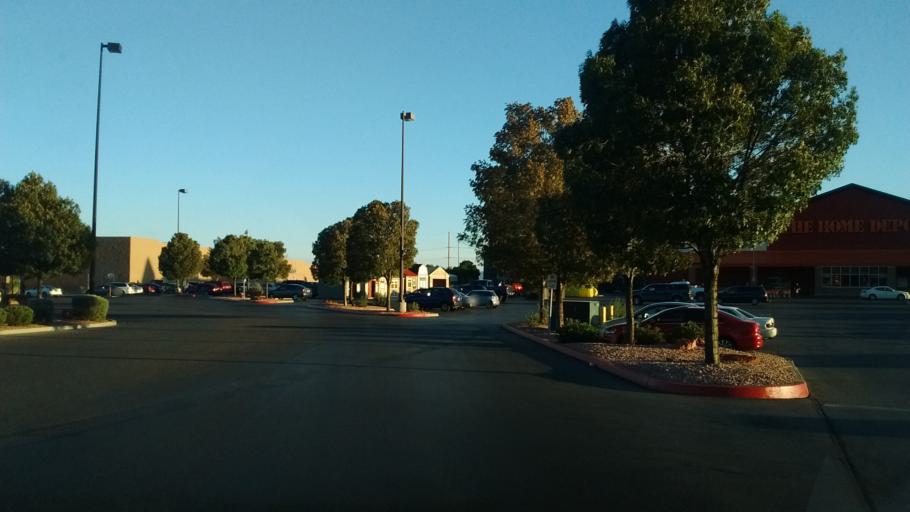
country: US
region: Utah
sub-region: Washington County
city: Washington
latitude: 37.1273
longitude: -113.5201
